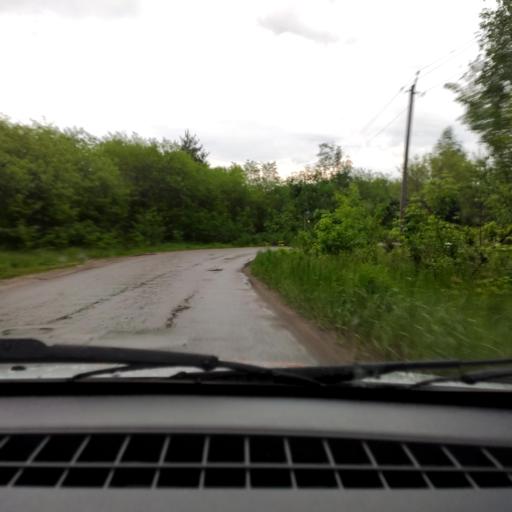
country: RU
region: Voronezj
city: Ramon'
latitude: 51.8482
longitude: 39.2312
